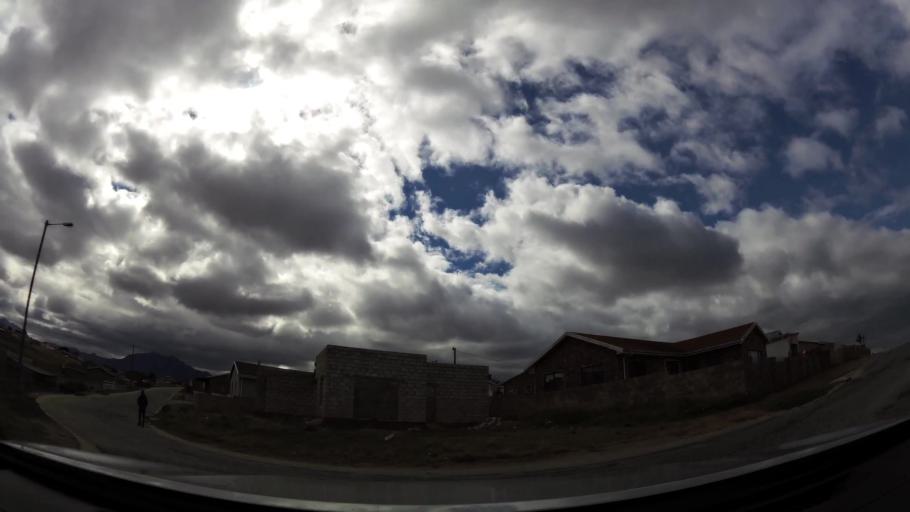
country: ZA
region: Western Cape
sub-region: Eden District Municipality
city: George
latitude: -34.0253
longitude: 22.4751
